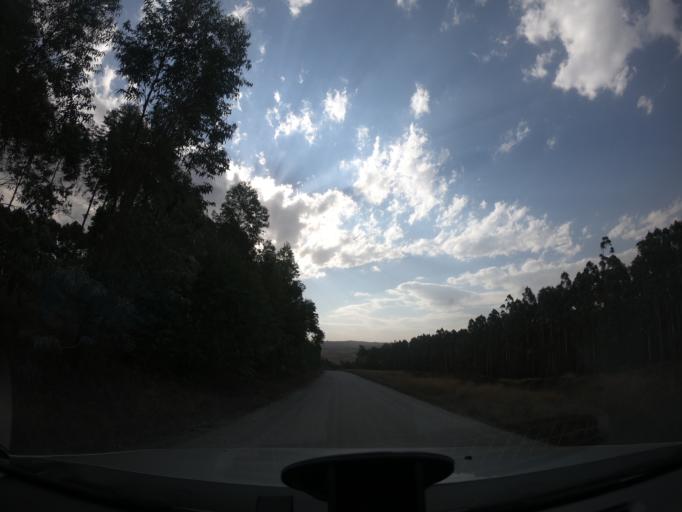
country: ZA
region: KwaZulu-Natal
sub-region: uMgungundlovu District Municipality
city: Howick
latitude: -29.4230
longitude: 30.1044
